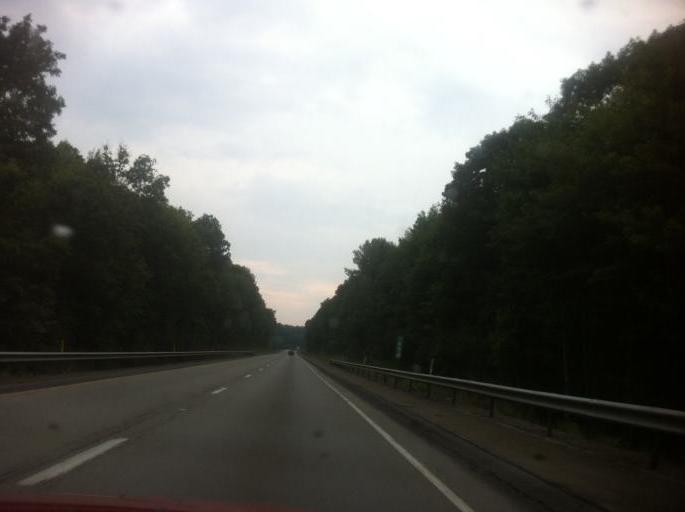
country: US
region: Pennsylvania
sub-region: Clarion County
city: Clarion
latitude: 41.1763
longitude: -79.2567
